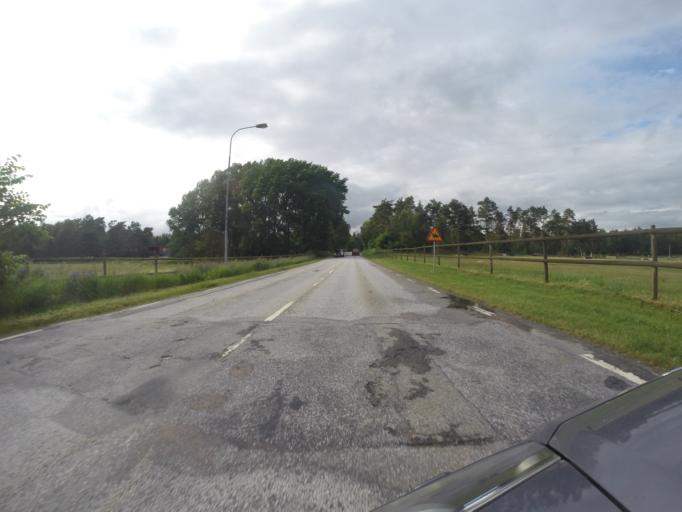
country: SE
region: Skane
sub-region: Kavlinge Kommun
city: Hofterup
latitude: 55.8032
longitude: 12.9854
